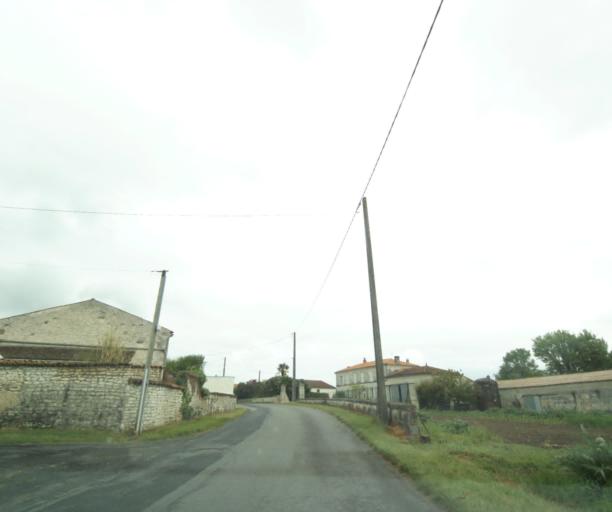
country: FR
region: Poitou-Charentes
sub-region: Departement de la Charente-Maritime
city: Chaniers
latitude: 45.6938
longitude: -0.5075
